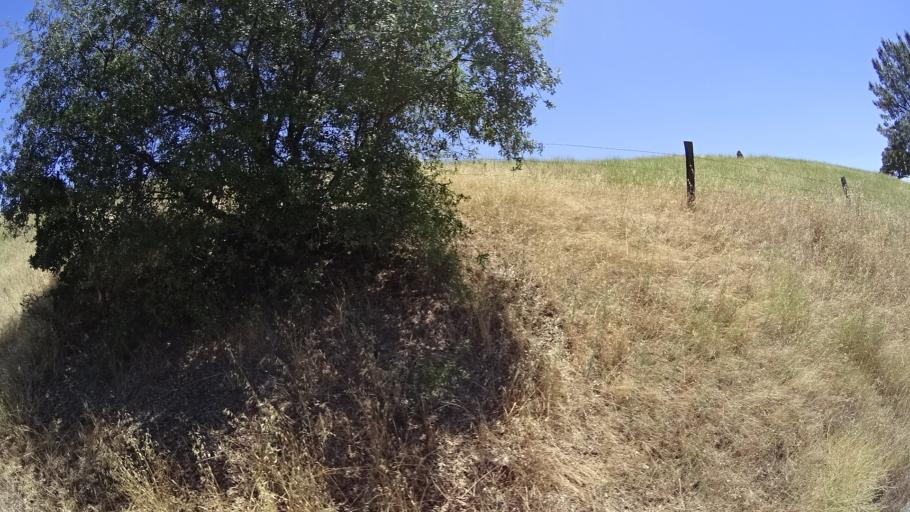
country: US
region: California
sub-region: Calaveras County
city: Valley Springs
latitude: 38.2389
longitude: -120.7891
